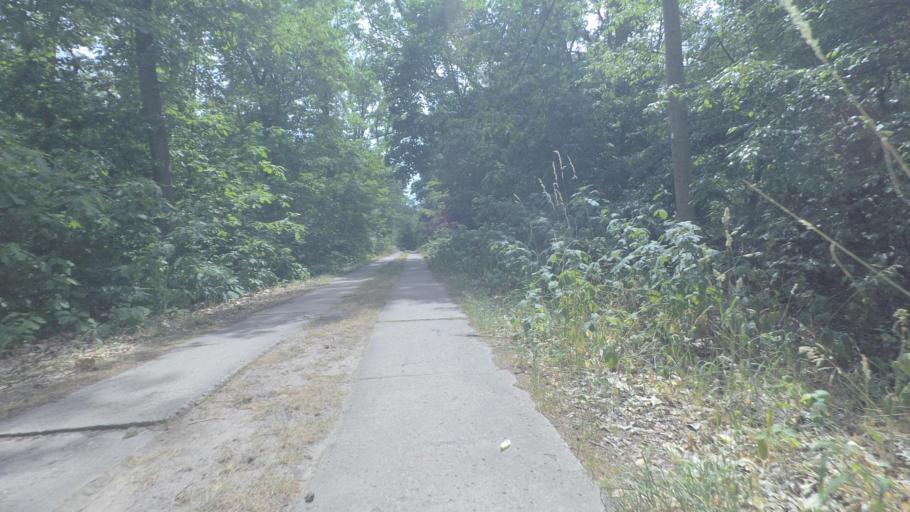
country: DE
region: Brandenburg
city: Stahnsdorf
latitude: 52.3417
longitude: 13.2264
